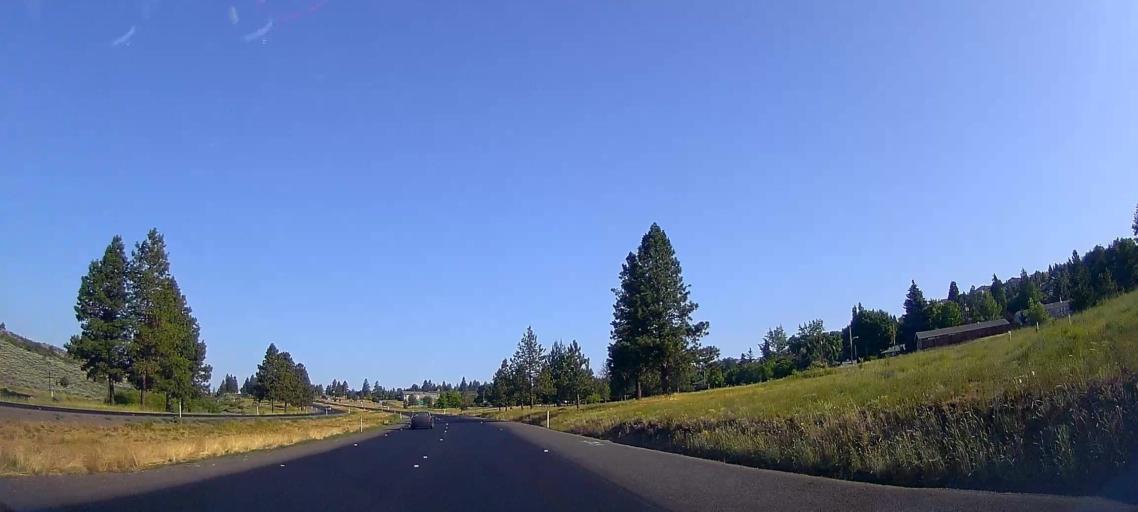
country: US
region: Oregon
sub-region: Klamath County
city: Klamath Falls
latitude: 42.2423
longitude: -121.7820
